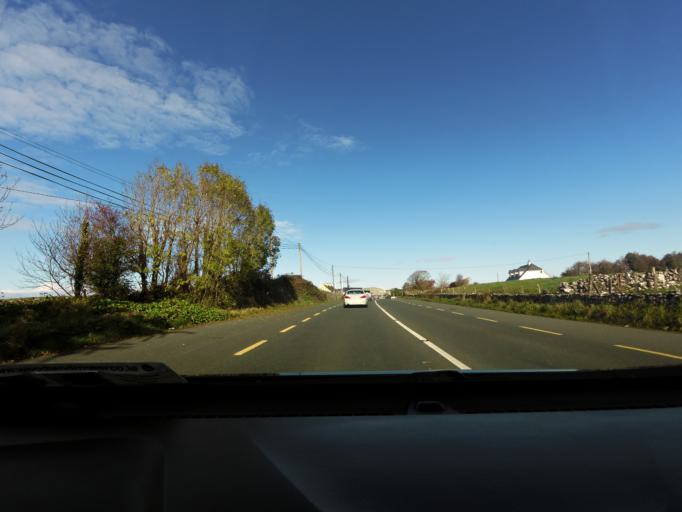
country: IE
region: Connaught
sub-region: County Galway
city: Moycullen
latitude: 53.4608
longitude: -9.1035
